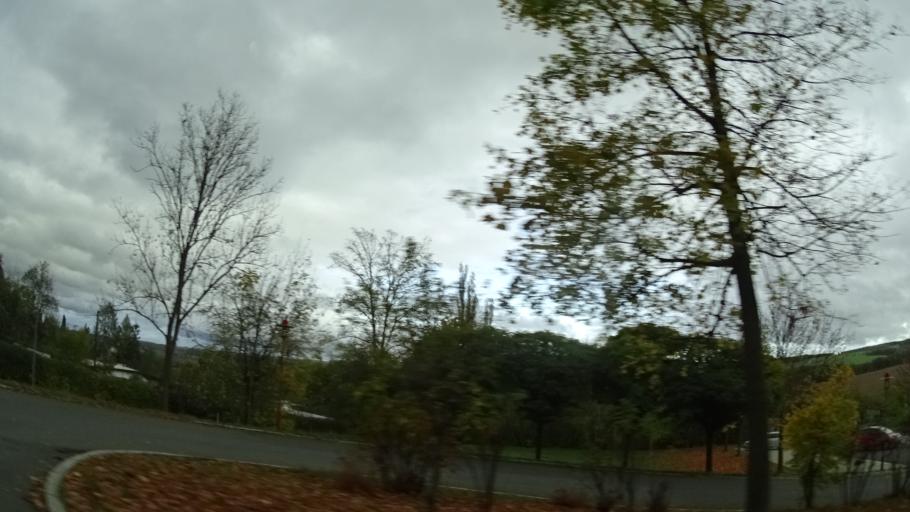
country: DE
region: Thuringia
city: Possneck
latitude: 50.6905
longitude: 11.6010
